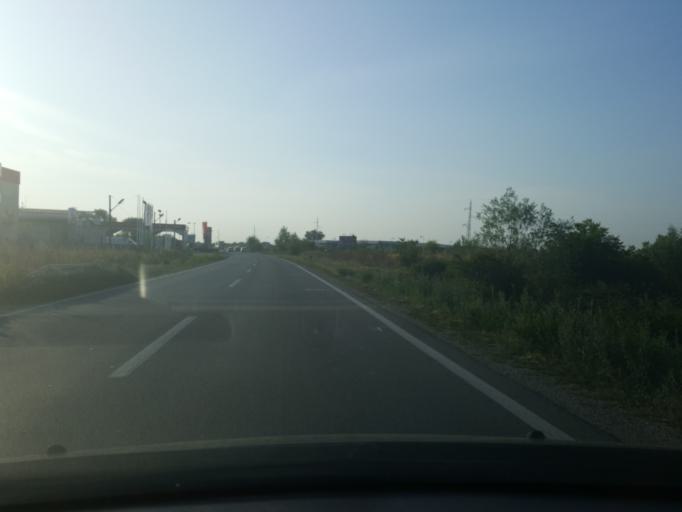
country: RS
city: Majur
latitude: 44.7615
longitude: 19.6422
